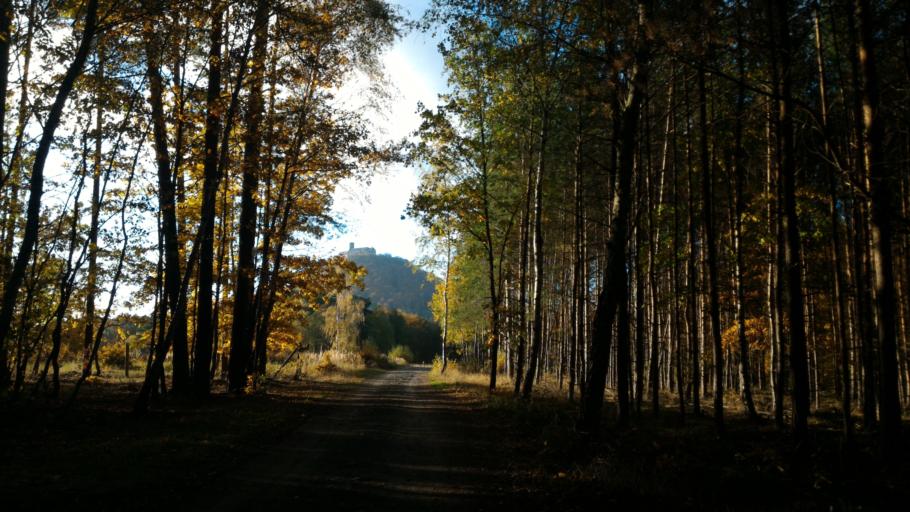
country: CZ
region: Central Bohemia
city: Bela pod Bezdezem
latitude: 50.5357
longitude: 14.7426
